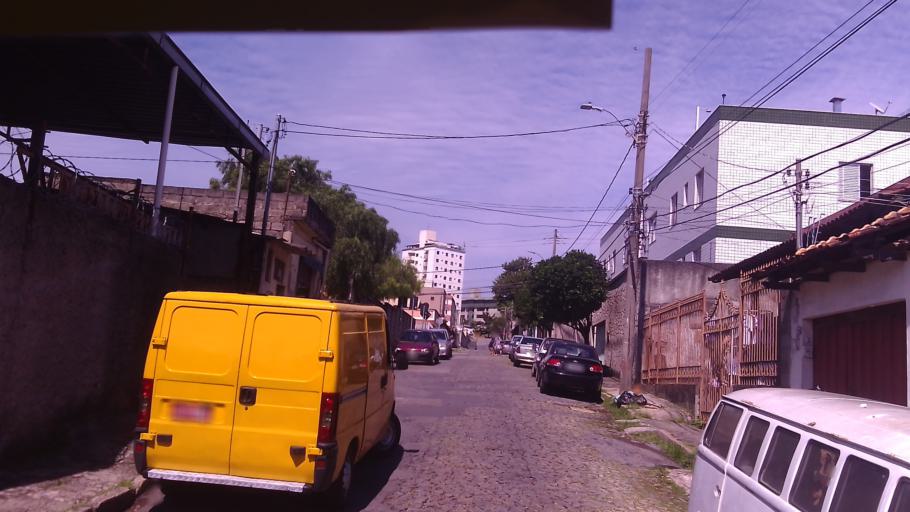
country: BR
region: Minas Gerais
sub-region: Contagem
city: Contagem
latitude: -19.9288
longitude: -43.9999
